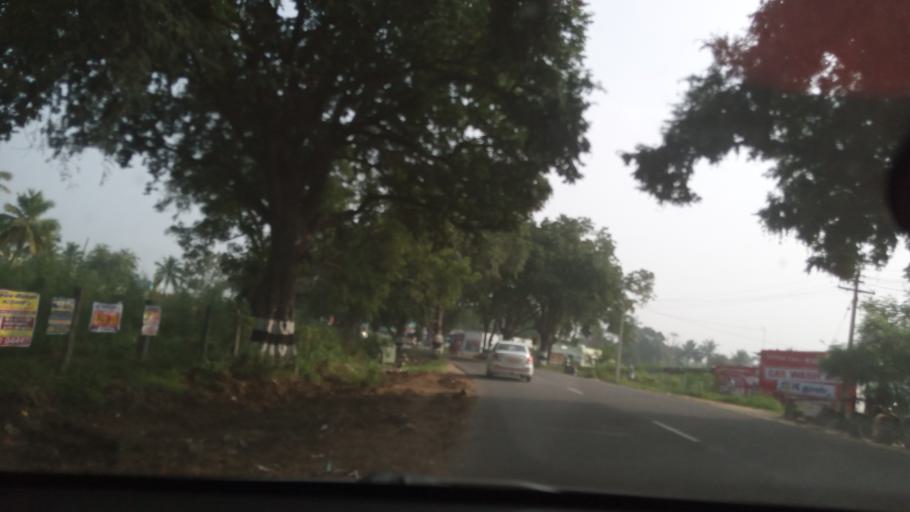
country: IN
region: Tamil Nadu
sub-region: Coimbatore
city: Periyanayakkanpalaiyam
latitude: 11.1505
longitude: 77.0469
